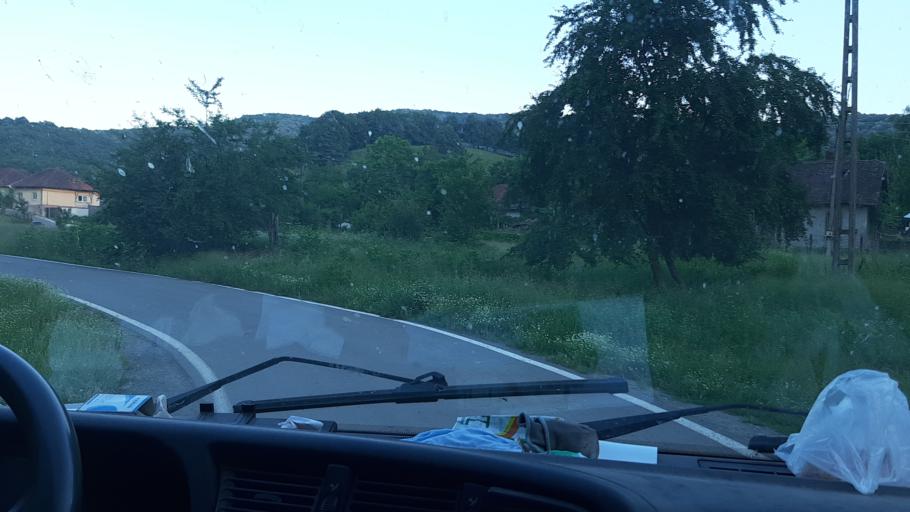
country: RO
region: Caras-Severin
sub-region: Municipiul Resita
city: Calnic
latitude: 45.3687
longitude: 21.7991
